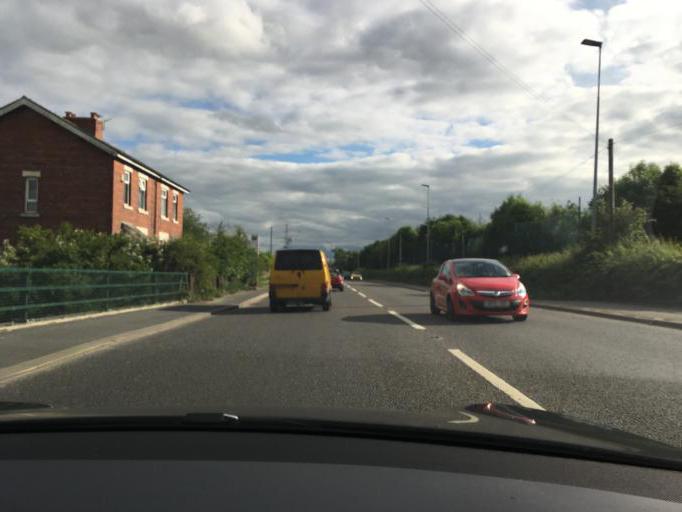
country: GB
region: England
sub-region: City and Borough of Salford
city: Irlam
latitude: 53.4620
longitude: -2.3985
